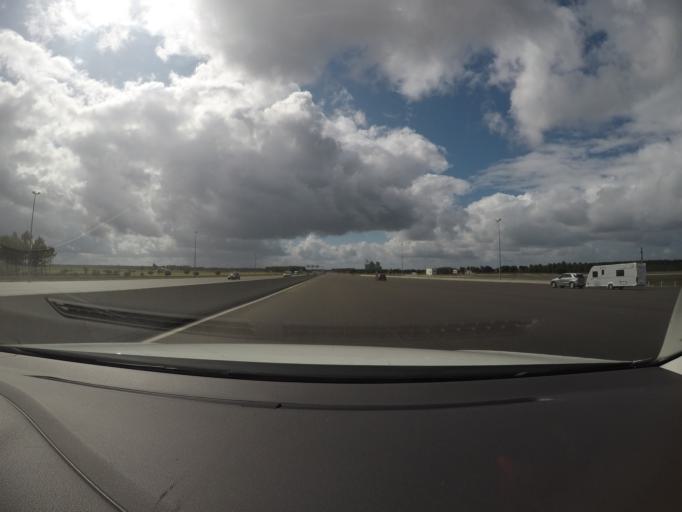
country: FR
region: Aquitaine
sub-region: Departement des Landes
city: Pissos
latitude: 44.3466
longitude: -0.8605
